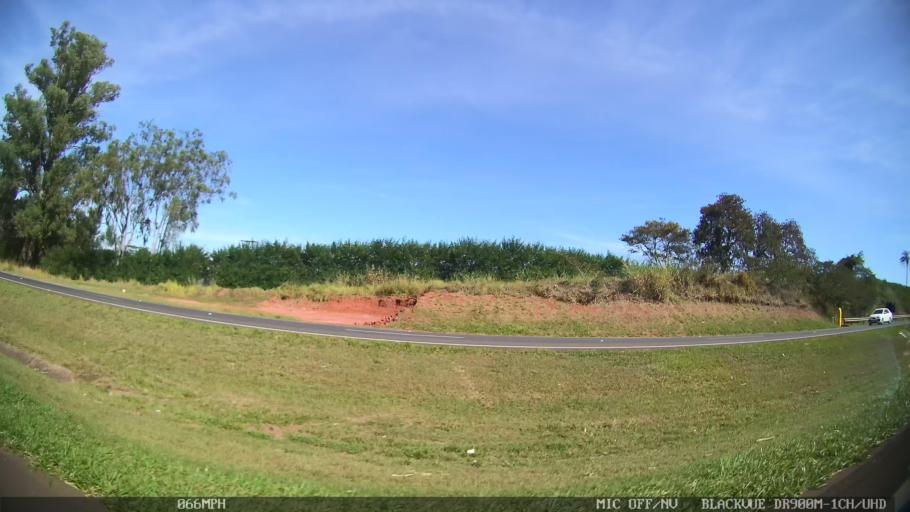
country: BR
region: Sao Paulo
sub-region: Porto Ferreira
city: Porto Ferreira
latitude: -21.8085
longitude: -47.5009
